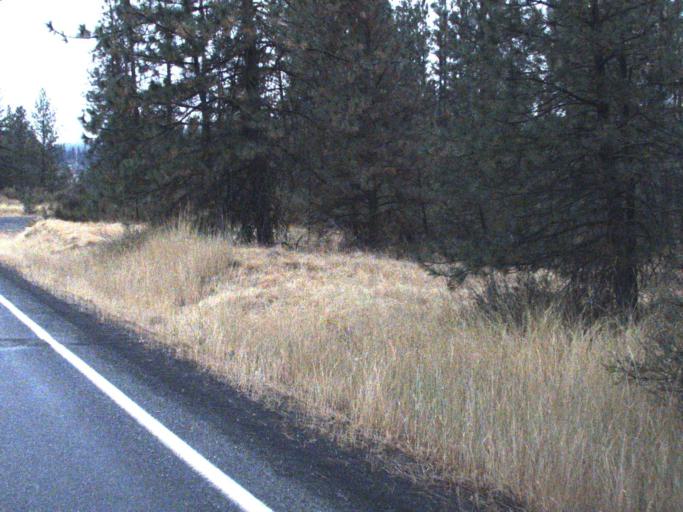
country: US
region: Washington
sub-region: Lincoln County
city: Davenport
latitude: 47.7895
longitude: -117.8900
